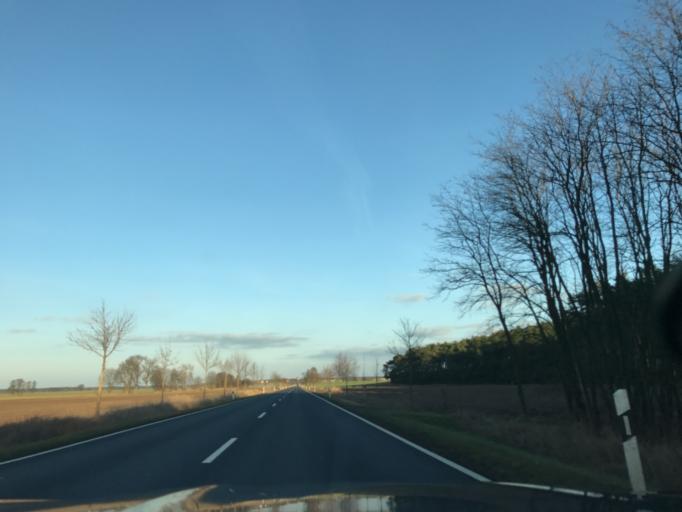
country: DE
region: Saxony-Anhalt
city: Burg bei Magdeburg
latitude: 52.2991
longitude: 11.9794
